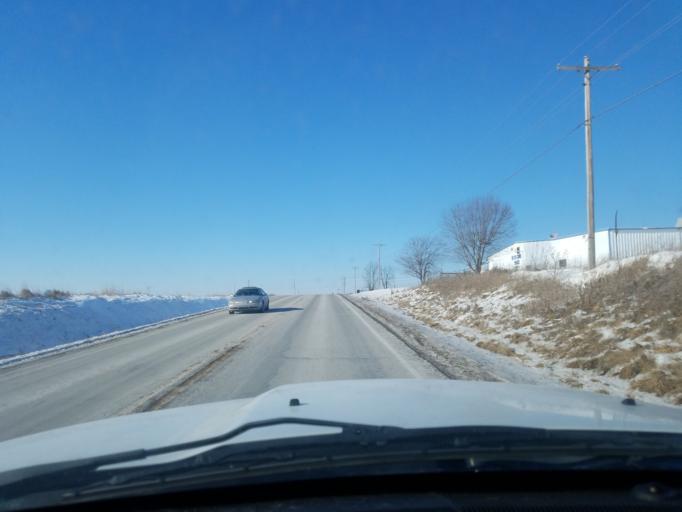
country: US
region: Indiana
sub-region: Noble County
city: Albion
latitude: 41.3959
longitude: -85.3927
